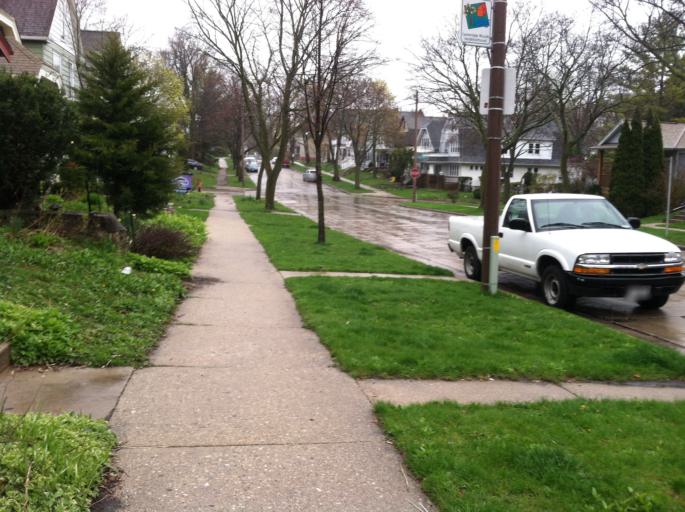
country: US
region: Wisconsin
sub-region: Milwaukee County
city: Shorewood
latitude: 43.0763
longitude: -87.8902
